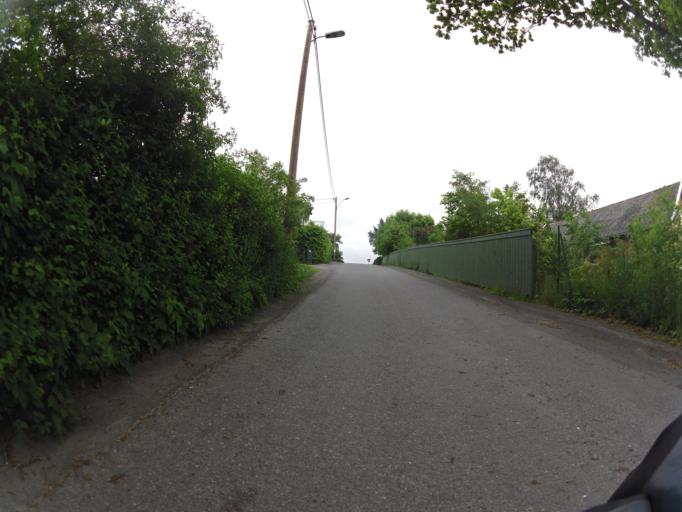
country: NO
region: Ostfold
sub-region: Moss
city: Moss
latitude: 59.4166
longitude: 10.6610
